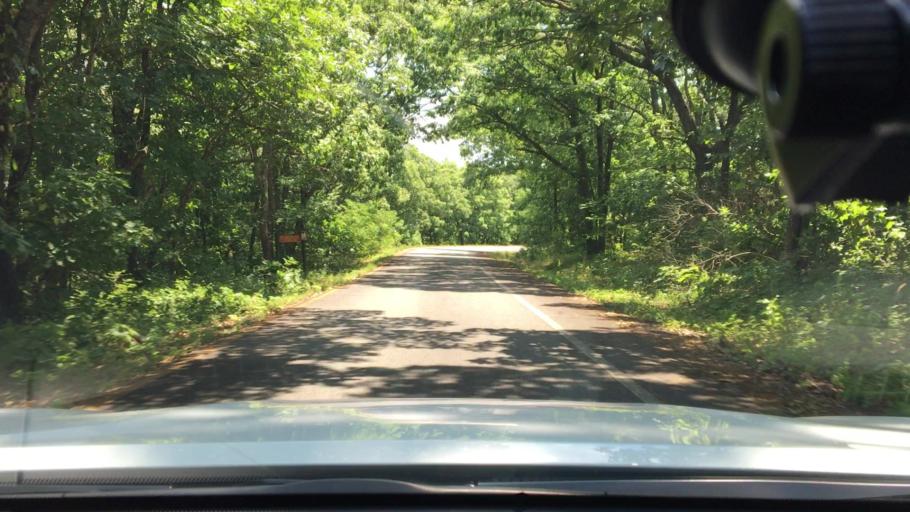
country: US
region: Arkansas
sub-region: Logan County
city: Paris
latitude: 35.1764
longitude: -93.6447
